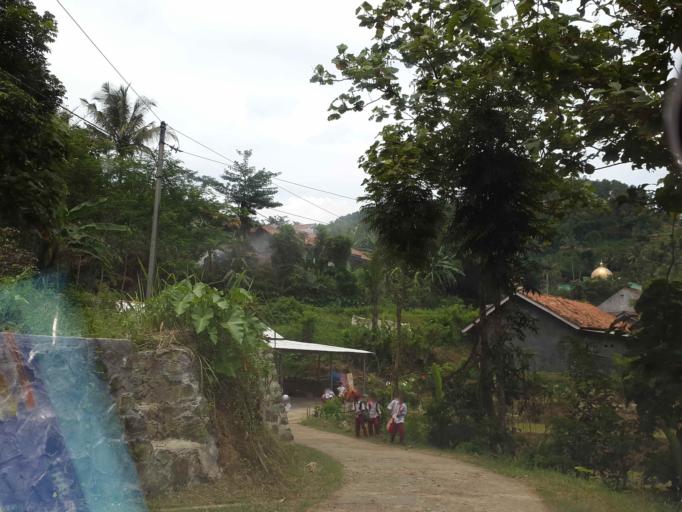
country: ID
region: Central Java
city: Muara
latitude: -7.2633
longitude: 108.8858
